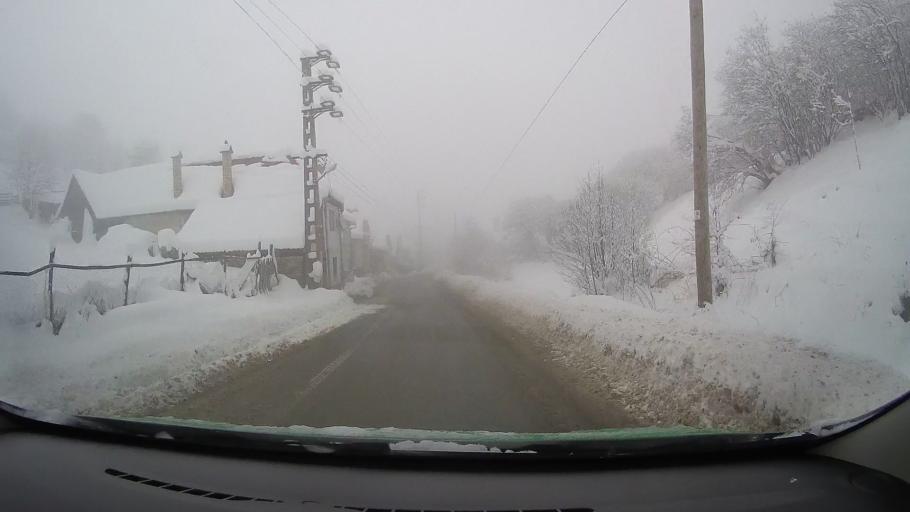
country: RO
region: Sibiu
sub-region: Comuna Poiana Sibiului
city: Poiana Sibiului
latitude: 45.8070
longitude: 23.7706
